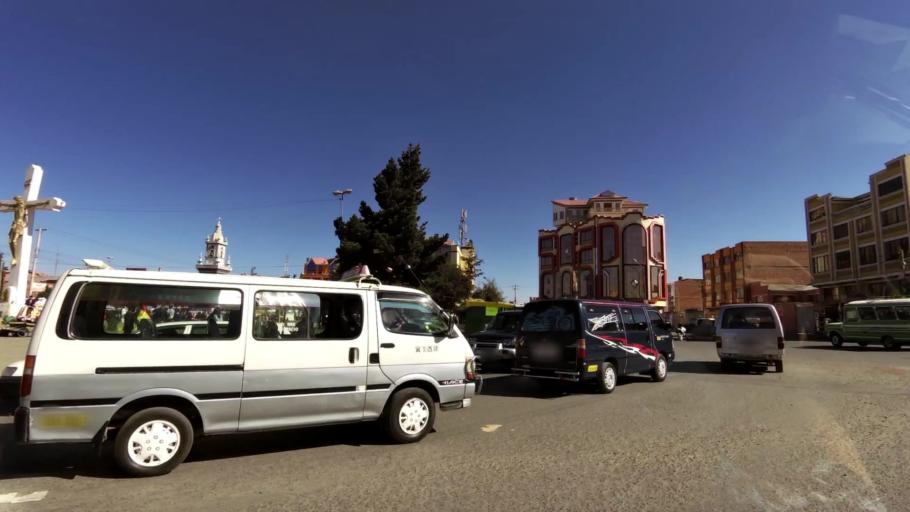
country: BO
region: La Paz
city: La Paz
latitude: -16.5251
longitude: -68.2002
